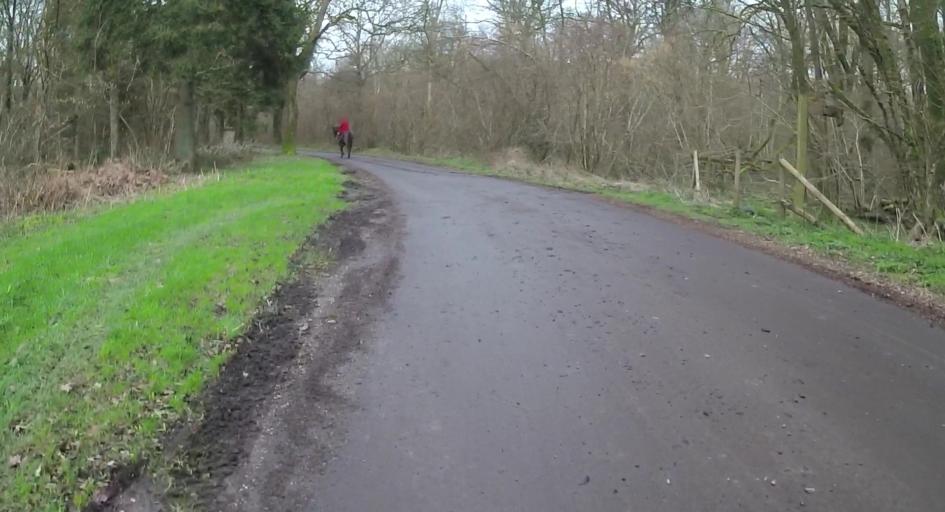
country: GB
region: England
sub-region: Hampshire
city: Kingsclere
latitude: 51.2820
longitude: -1.2027
